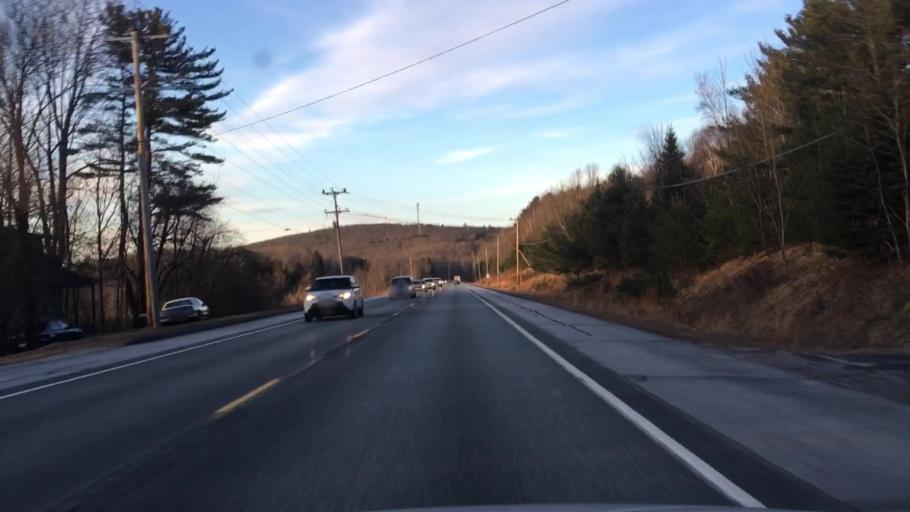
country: US
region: Maine
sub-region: Hancock County
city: Dedham
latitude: 44.7102
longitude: -68.6025
